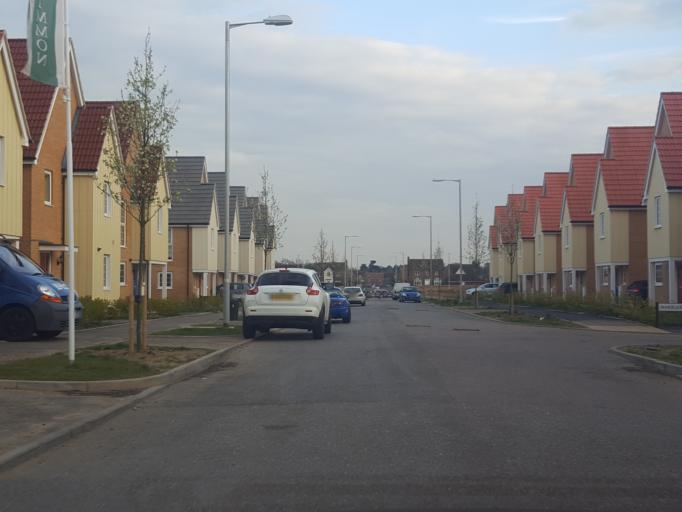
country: GB
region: England
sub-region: Essex
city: Eight Ash Green
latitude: 51.8816
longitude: 0.8286
